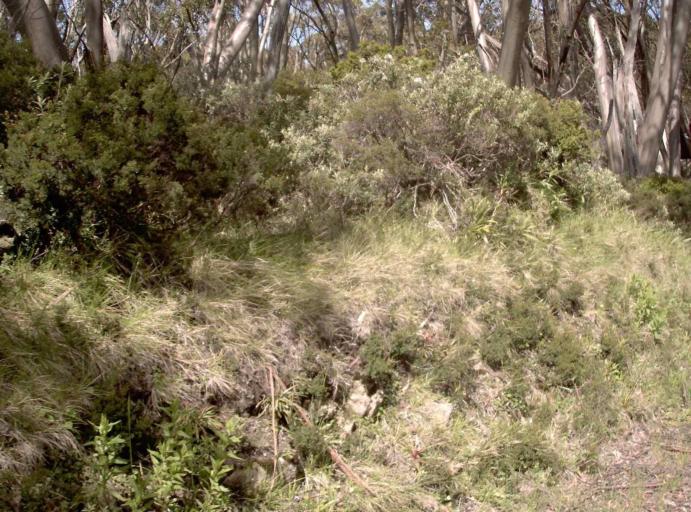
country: AU
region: Victoria
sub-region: Latrobe
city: Moe
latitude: -37.8390
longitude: 146.2612
